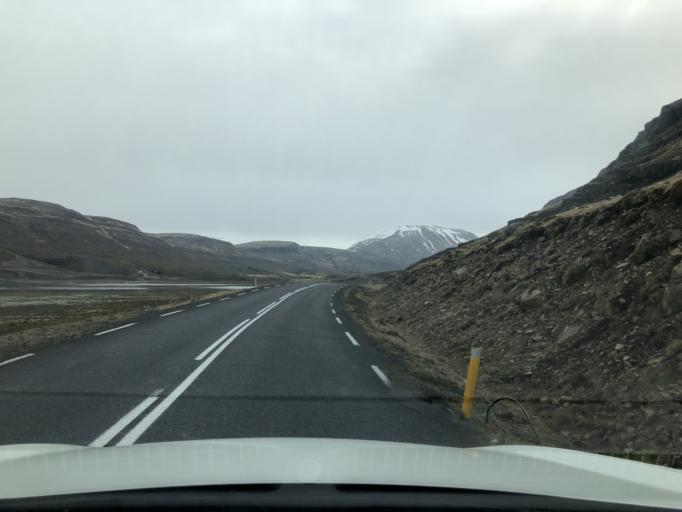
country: IS
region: Capital Region
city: Mosfellsbaer
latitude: 64.3796
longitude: -21.3784
